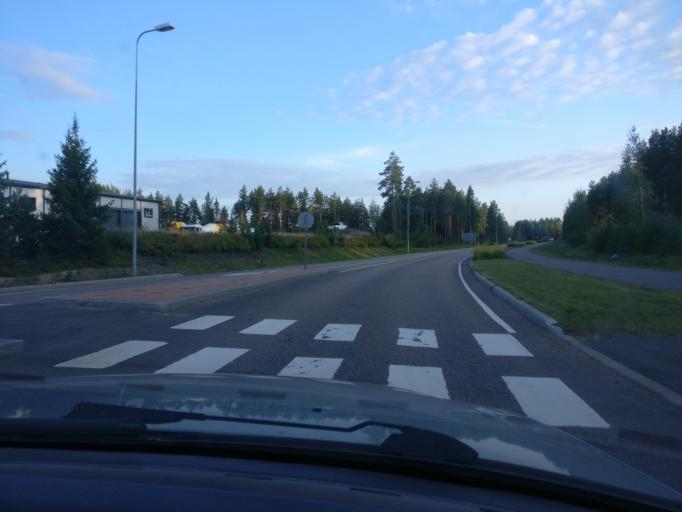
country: FI
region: Kymenlaakso
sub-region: Kotka-Hamina
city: Broby
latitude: 60.5013
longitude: 26.7411
